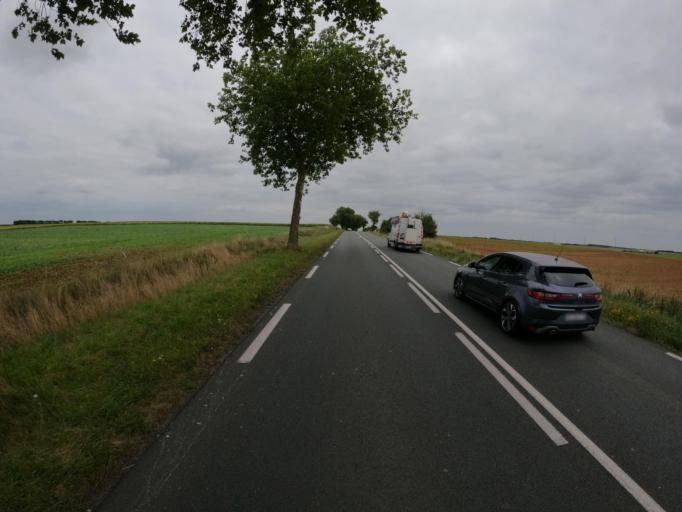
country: FR
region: Pays de la Loire
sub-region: Departement de la Vendee
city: Saint-Martin-sous-Mouzeuil
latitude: 46.5221
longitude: -0.9875
